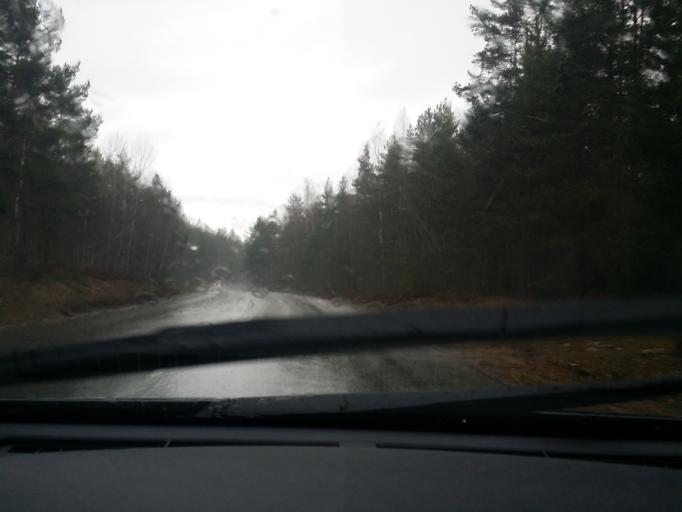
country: SE
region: Soedermanland
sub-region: Eskilstuna Kommun
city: Arla
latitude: 59.3553
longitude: 16.6880
